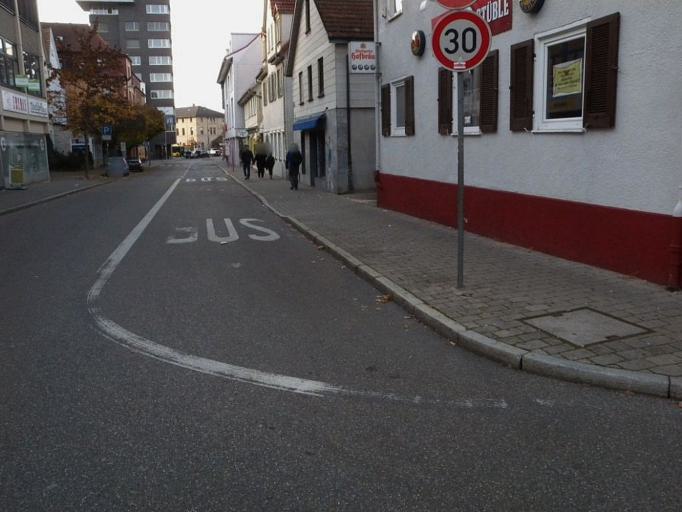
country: DE
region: Baden-Wuerttemberg
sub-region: Regierungsbezirk Stuttgart
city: Schorndorf
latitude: 48.8064
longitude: 9.5288
